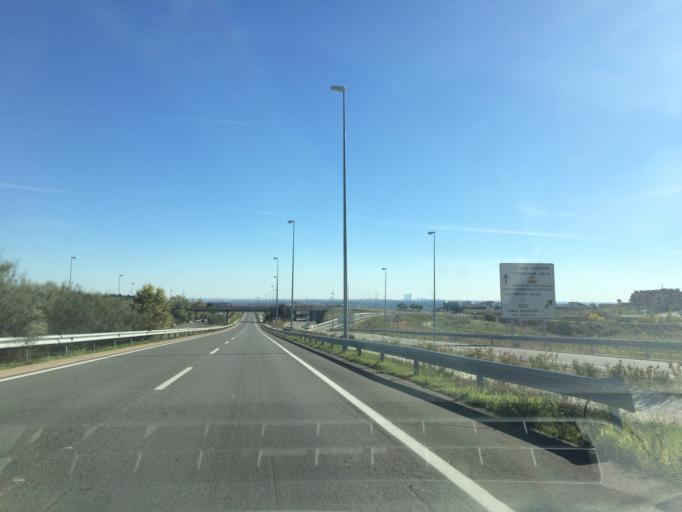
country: ES
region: Madrid
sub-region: Provincia de Madrid
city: Colmenar Viejo
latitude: 40.6675
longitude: -3.7551
